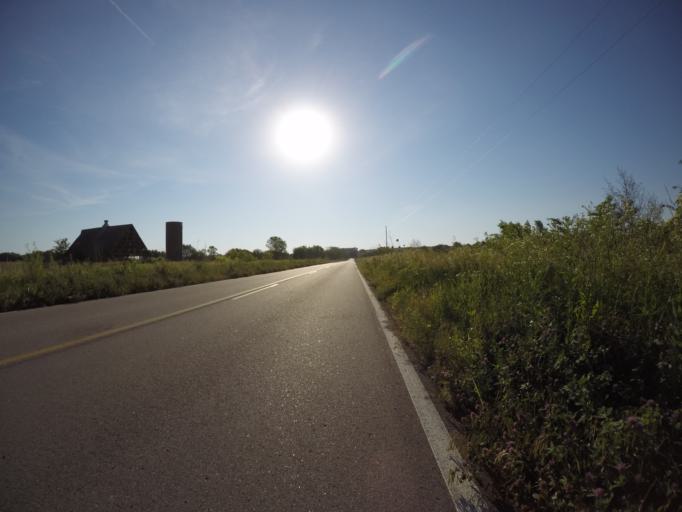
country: US
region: Nebraska
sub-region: Gage County
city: Wymore
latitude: 40.1028
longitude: -96.5087
